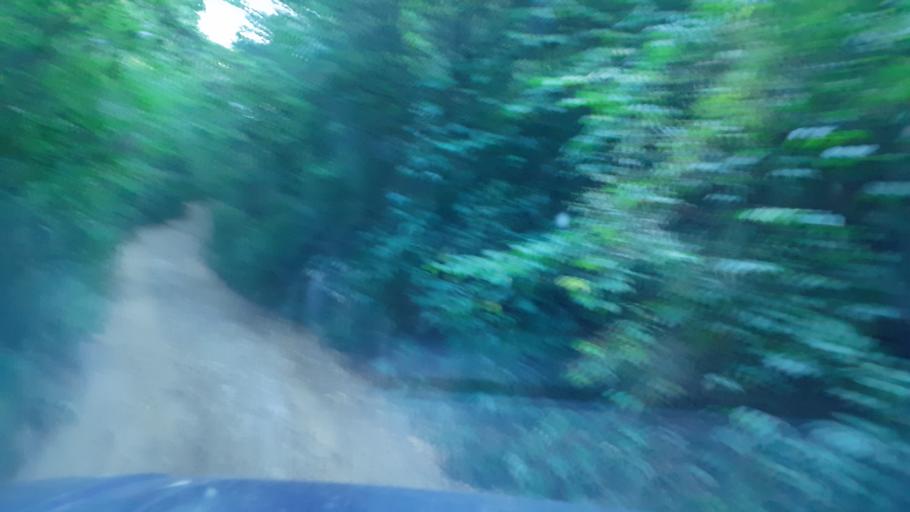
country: RU
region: Krasnodarskiy
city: Chernomorskiy
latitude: 44.6582
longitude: 38.4590
